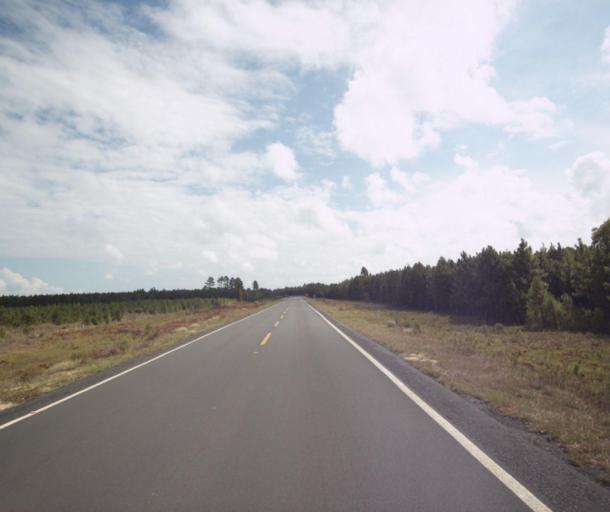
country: BR
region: Rio Grande do Sul
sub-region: Sao Lourenco Do Sul
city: Sao Lourenco do Sul
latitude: -31.4620
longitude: -51.2290
